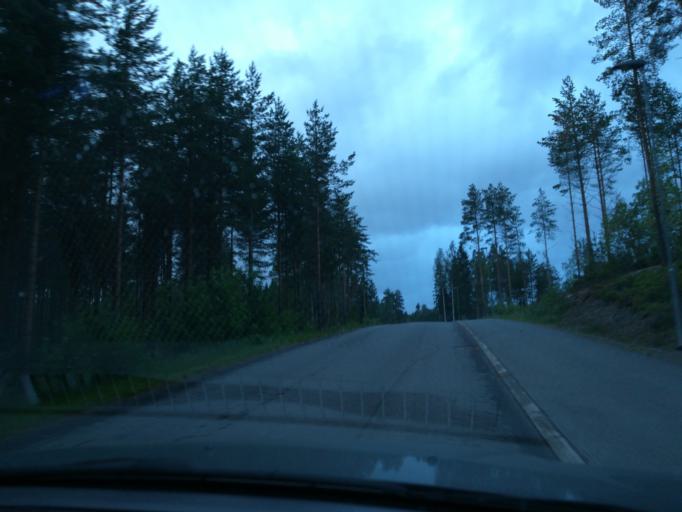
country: FI
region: Southern Savonia
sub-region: Mikkeli
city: Ristiina
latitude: 61.4892
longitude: 27.2780
